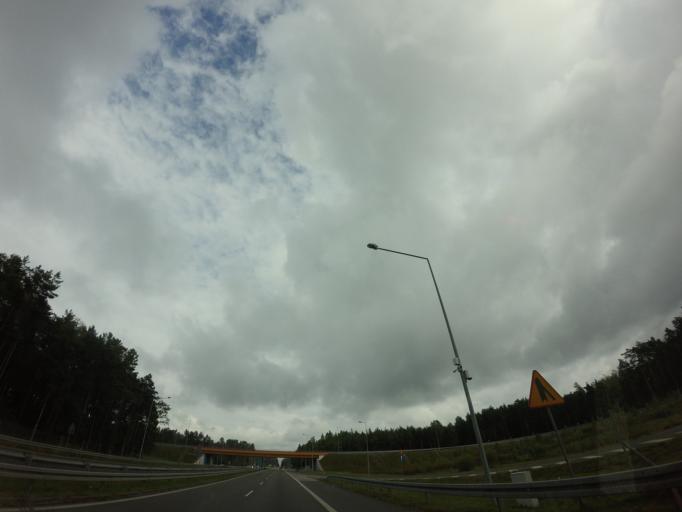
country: PL
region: West Pomeranian Voivodeship
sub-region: Powiat goleniowski
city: Goleniow
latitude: 53.6238
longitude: 14.8189
